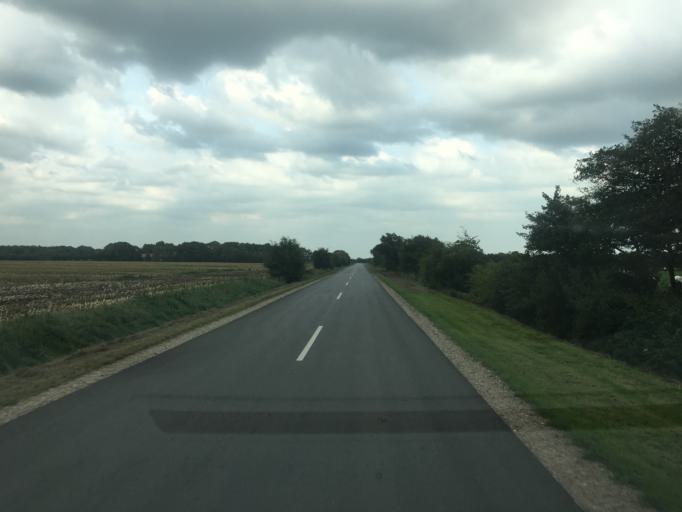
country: DK
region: South Denmark
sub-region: Tonder Kommune
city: Logumkloster
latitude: 55.0618
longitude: 9.0416
